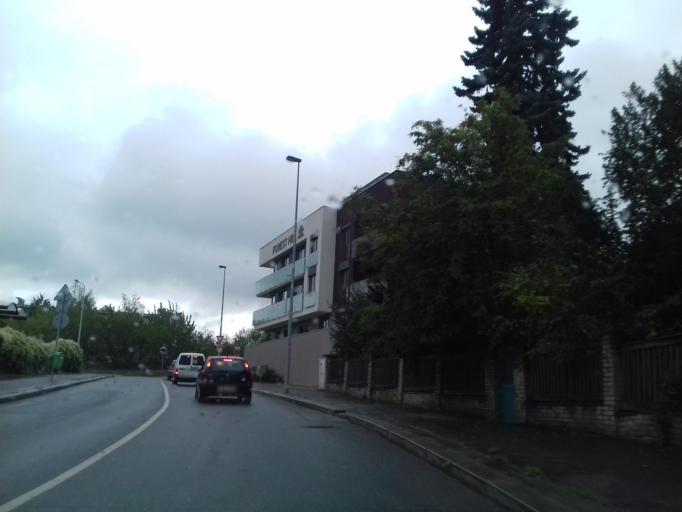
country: CZ
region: Praha
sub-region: Praha 1
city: Mala Strana
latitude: 50.0561
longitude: 14.3652
